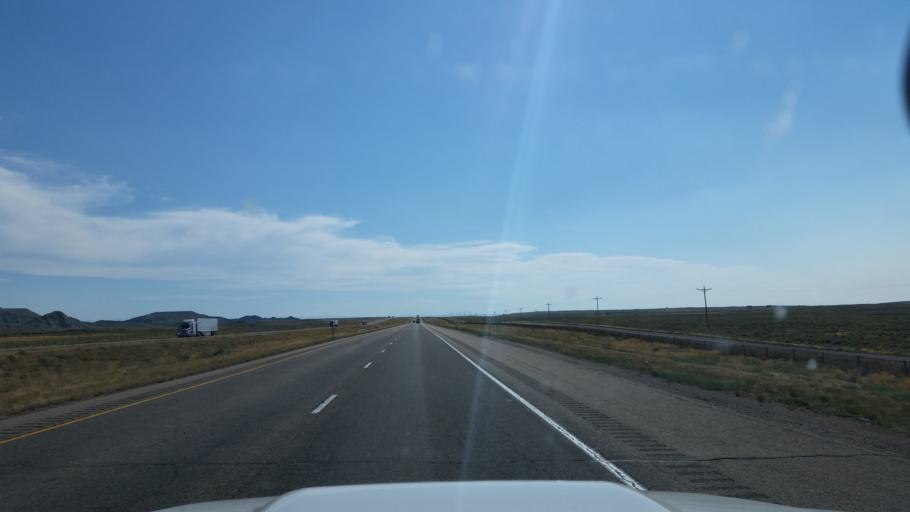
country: US
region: Wyoming
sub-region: Uinta County
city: Lyman
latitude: 41.4464
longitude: -110.0818
